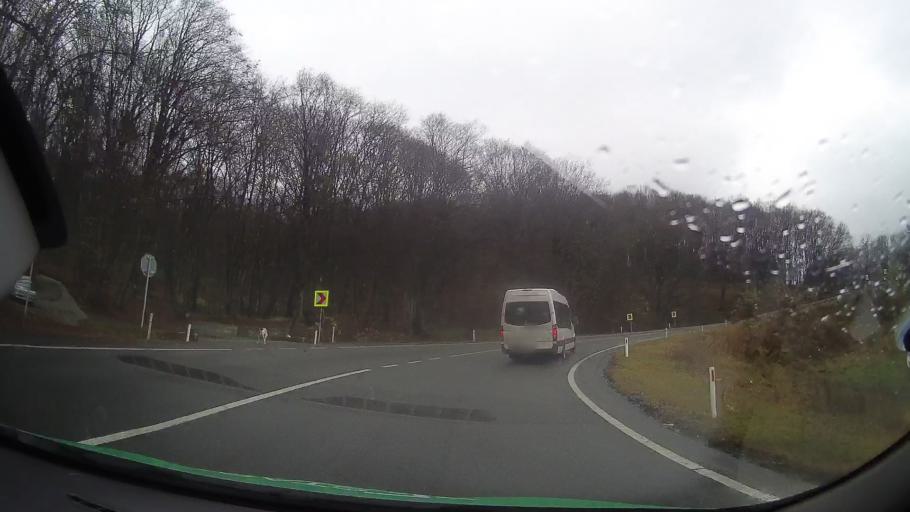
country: RO
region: Bistrita-Nasaud
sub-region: Comuna Sieu-Magherus
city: Sieu-Magherus
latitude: 47.0426
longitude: 24.4207
